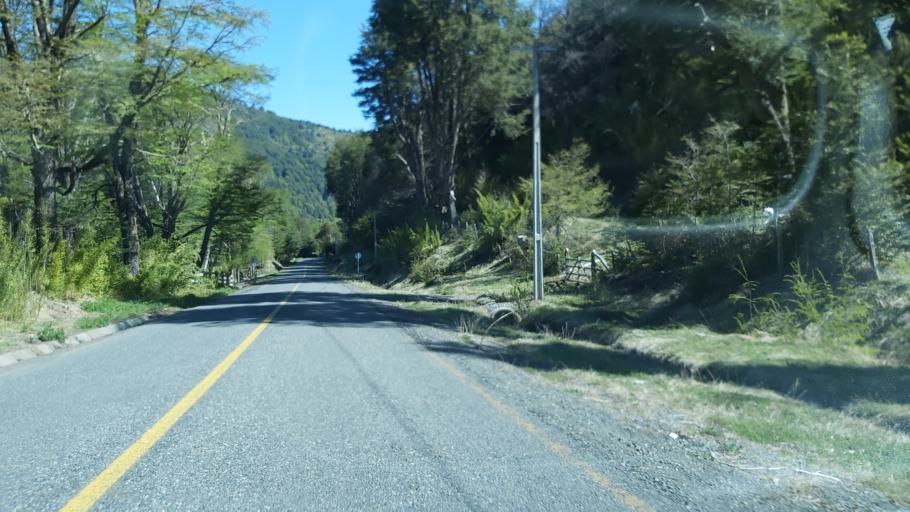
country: CL
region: Araucania
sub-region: Provincia de Cautin
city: Vilcun
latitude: -38.4582
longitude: -71.5161
